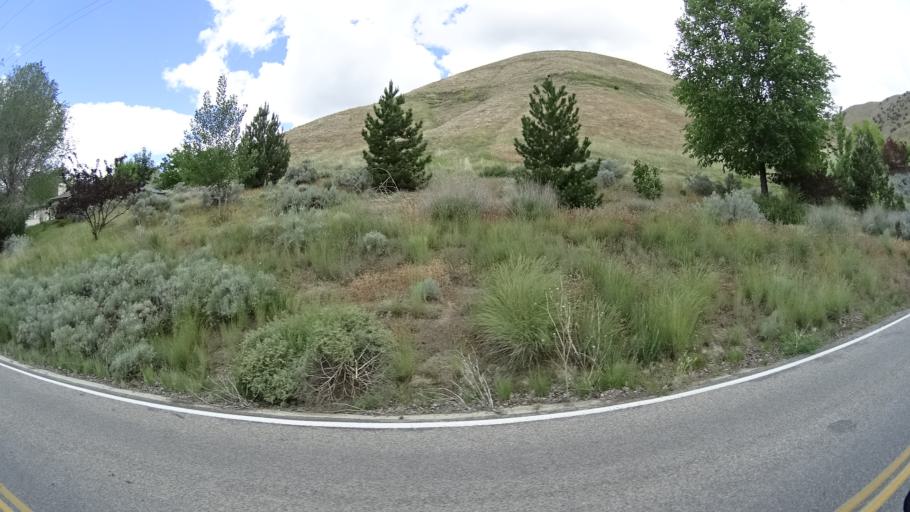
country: US
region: Idaho
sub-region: Ada County
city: Garden City
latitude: 43.6588
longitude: -116.2320
